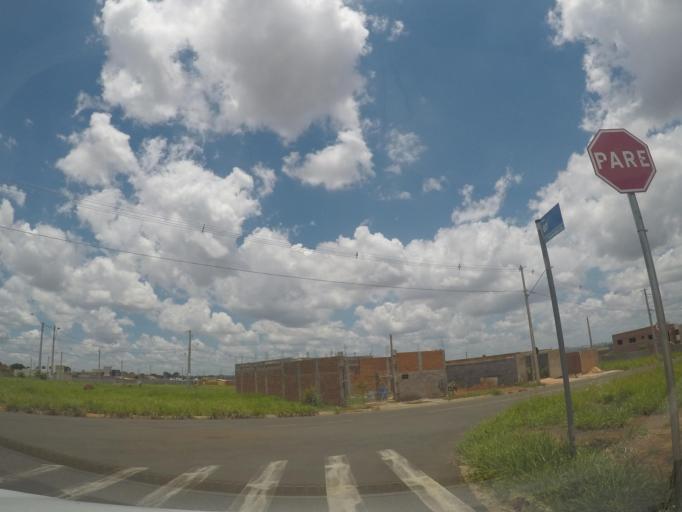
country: BR
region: Sao Paulo
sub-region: Hortolandia
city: Hortolandia
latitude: -22.8380
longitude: -47.2250
